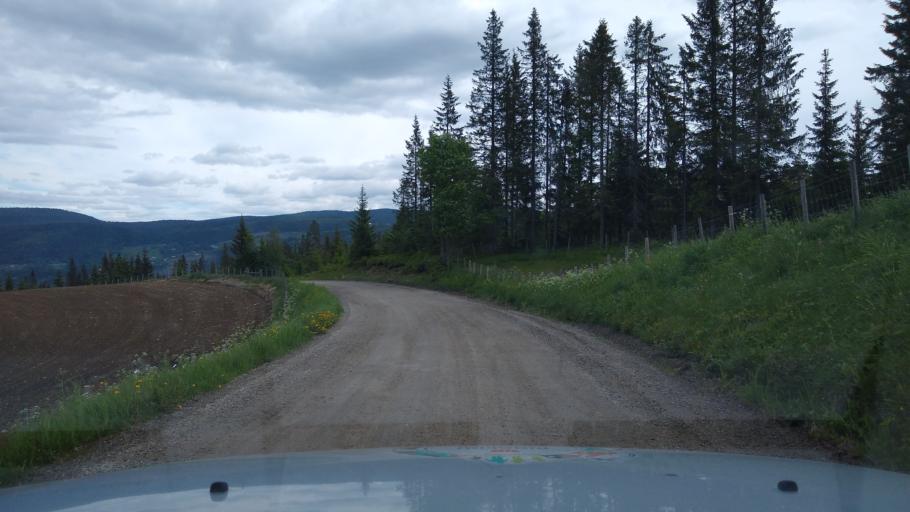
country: NO
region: Oppland
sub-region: Ringebu
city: Ringebu
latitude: 61.4935
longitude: 10.1441
